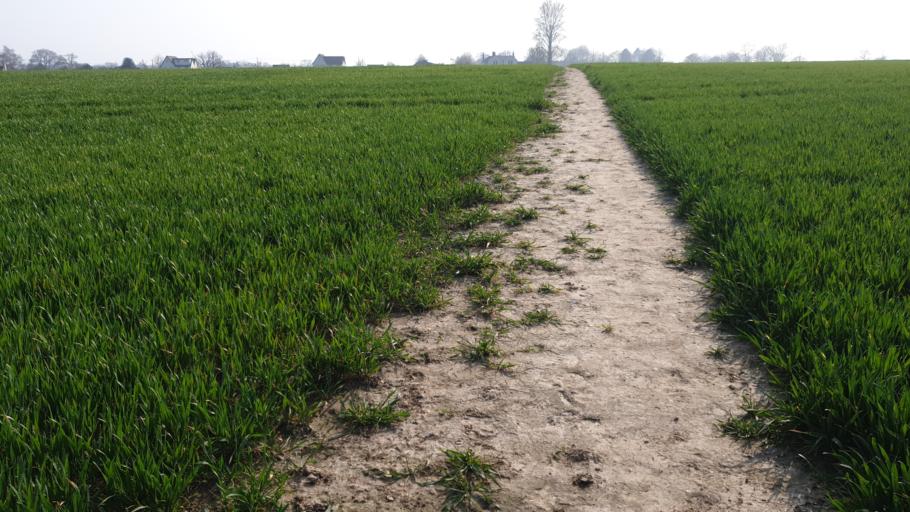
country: GB
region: England
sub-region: Essex
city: Great Bentley
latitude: 51.8842
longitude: 1.1188
